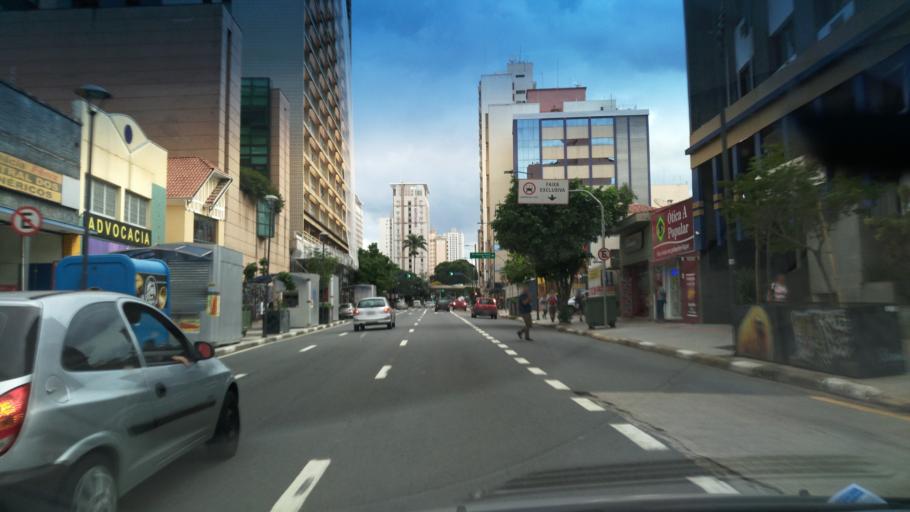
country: BR
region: Sao Paulo
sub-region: Campinas
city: Campinas
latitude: -22.9085
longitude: -47.0578
